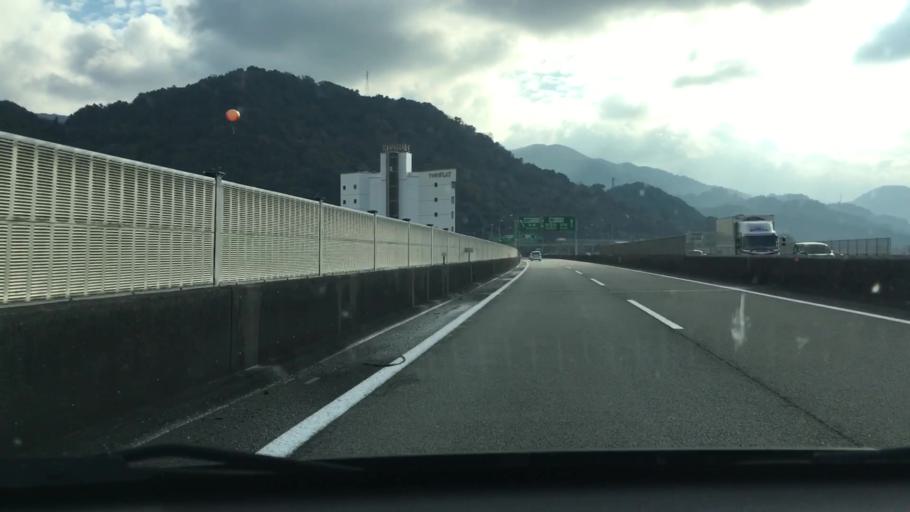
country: JP
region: Kumamoto
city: Yatsushiro
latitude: 32.5083
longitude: 130.6466
